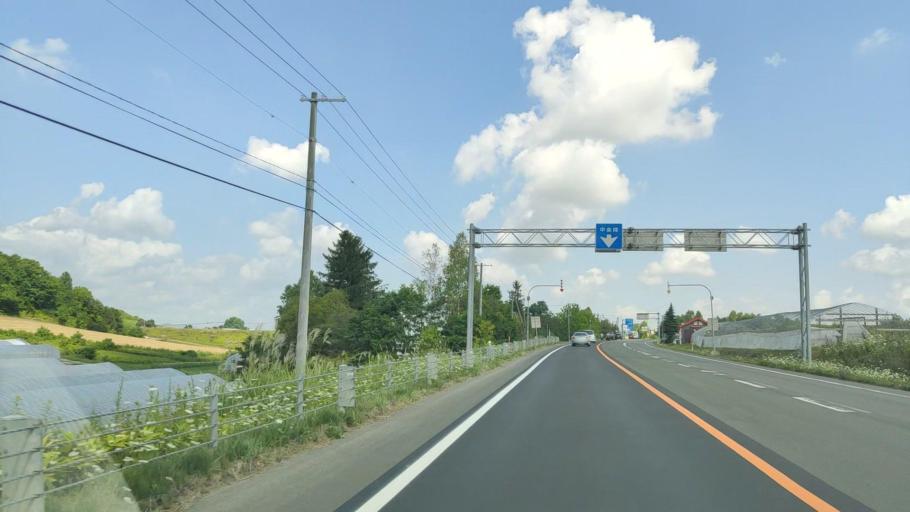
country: JP
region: Hokkaido
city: Shimo-furano
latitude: 43.5405
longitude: 142.4388
